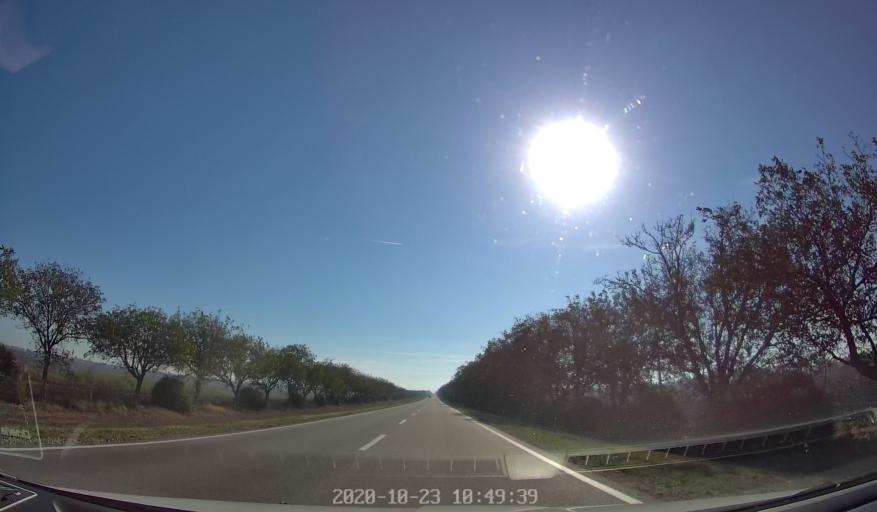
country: MD
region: Stefan-Voda
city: Stefan Voda
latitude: 46.5642
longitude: 29.6224
